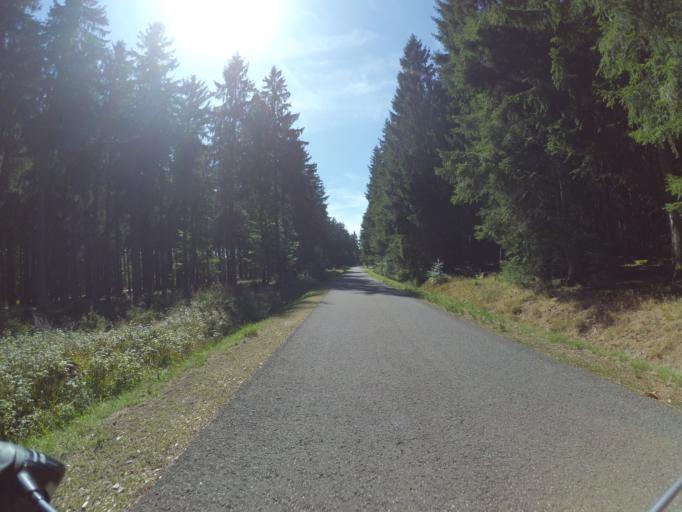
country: DE
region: Rheinland-Pfalz
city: Borfink
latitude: 49.7195
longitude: 7.0806
